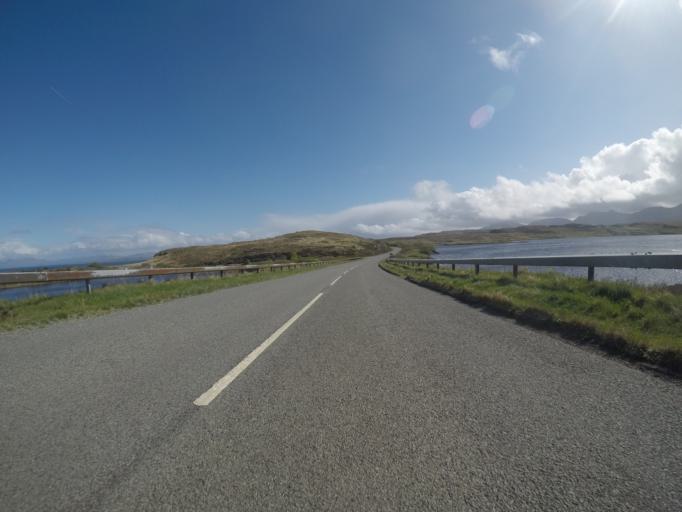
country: GB
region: Scotland
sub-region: Highland
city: Portree
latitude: 57.6104
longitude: -6.1753
